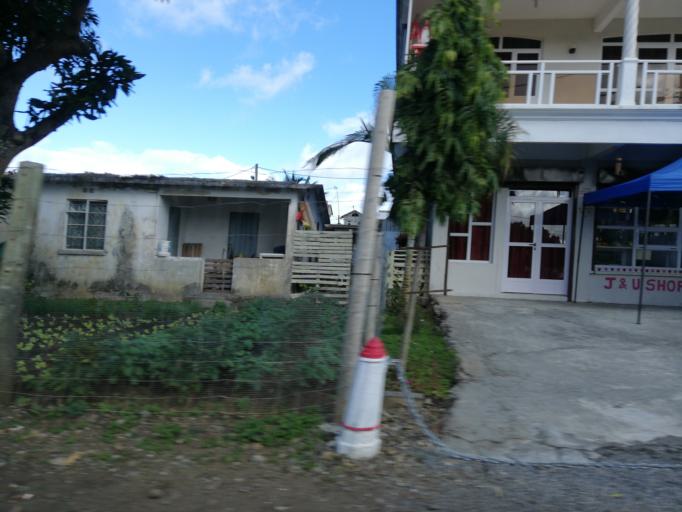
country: MU
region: Flacq
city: Bel Air Riviere Seche
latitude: -20.2617
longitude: 57.7436
